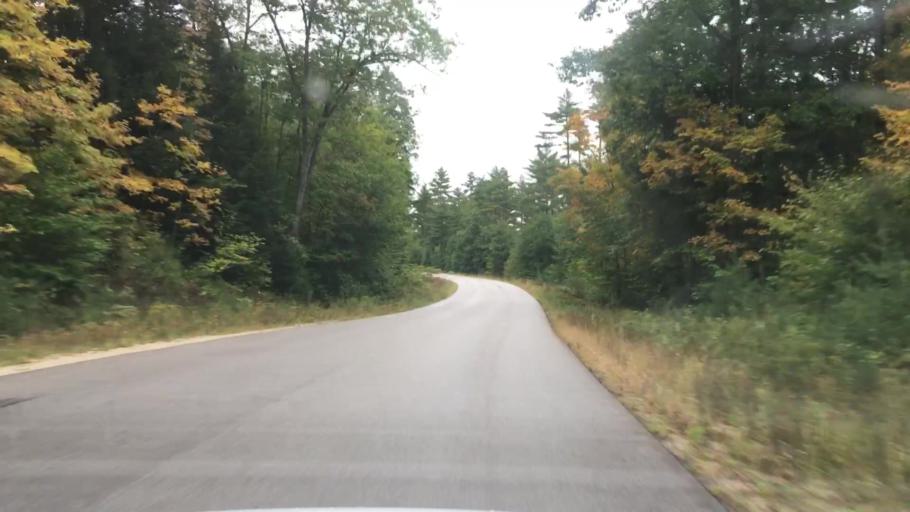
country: US
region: Maine
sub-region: Cumberland County
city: Harrison
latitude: 44.0228
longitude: -70.5893
